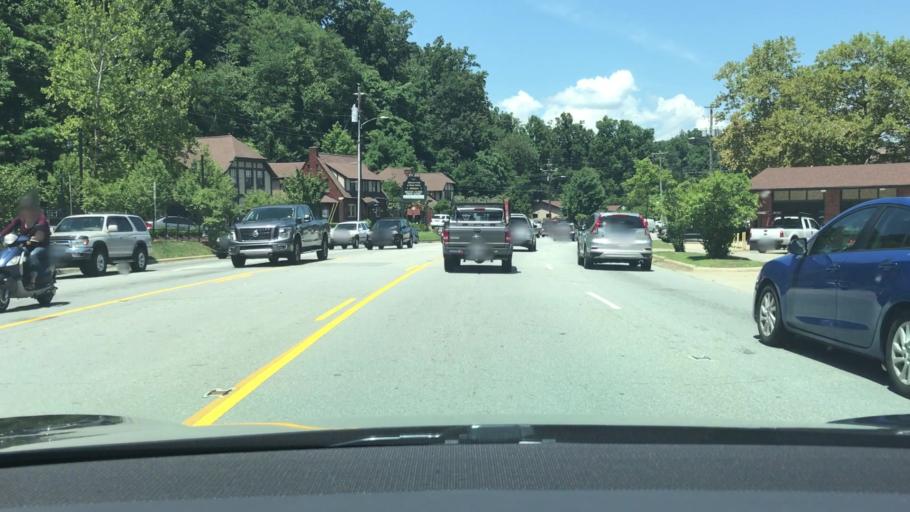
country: US
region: North Carolina
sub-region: Buncombe County
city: Biltmore Forest
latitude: 35.5652
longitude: -82.5433
